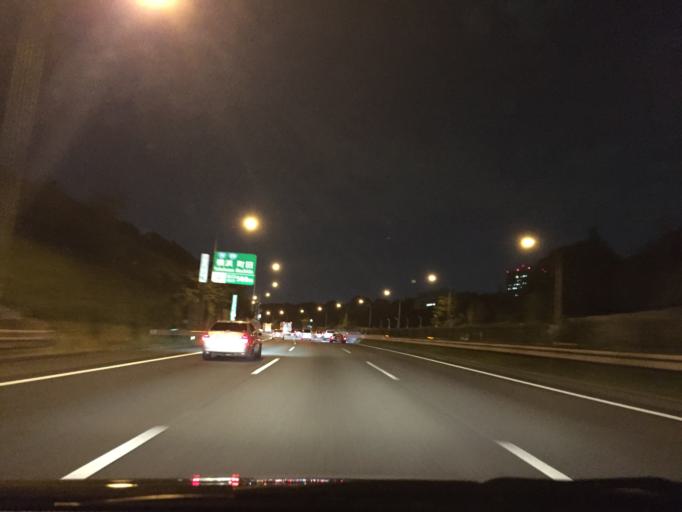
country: JP
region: Tokyo
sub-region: Machida-shi
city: Machida
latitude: 35.5141
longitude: 139.4909
